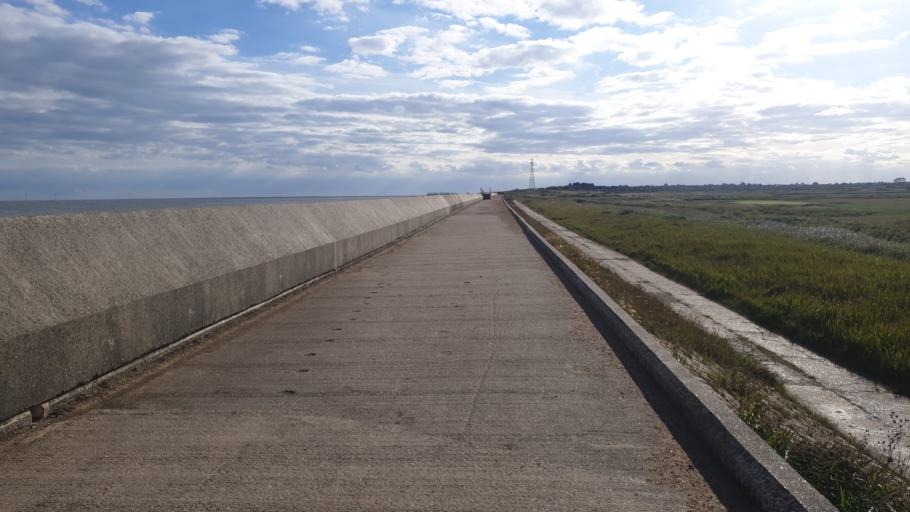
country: GB
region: England
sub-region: Essex
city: Frinton-on-Sea
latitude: 51.8166
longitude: 1.2307
